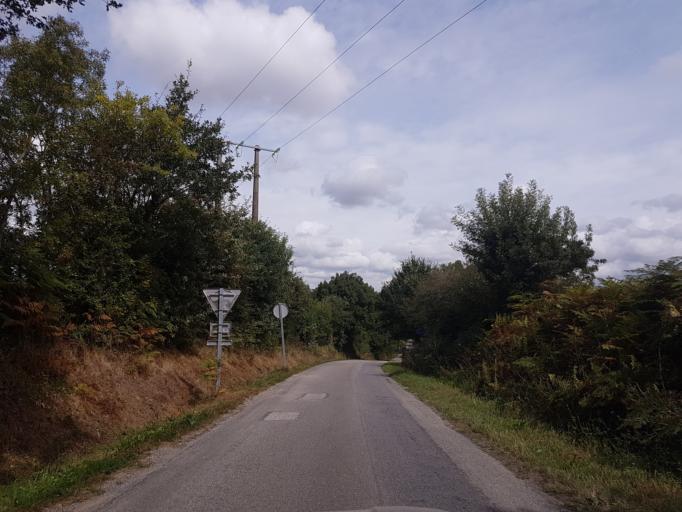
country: FR
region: Pays de la Loire
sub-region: Departement de la Loire-Atlantique
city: Petit-Mars
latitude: 47.3885
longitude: -1.4330
